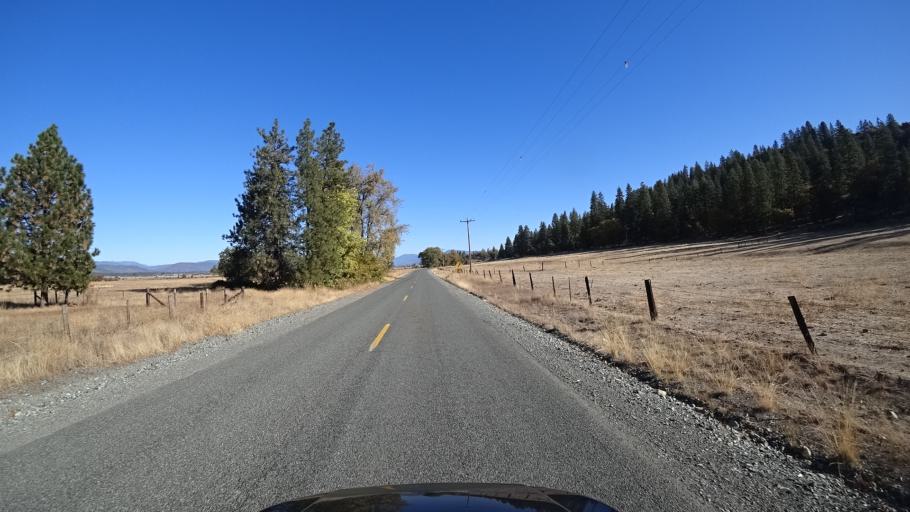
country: US
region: California
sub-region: Siskiyou County
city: Yreka
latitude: 41.4676
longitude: -122.8829
